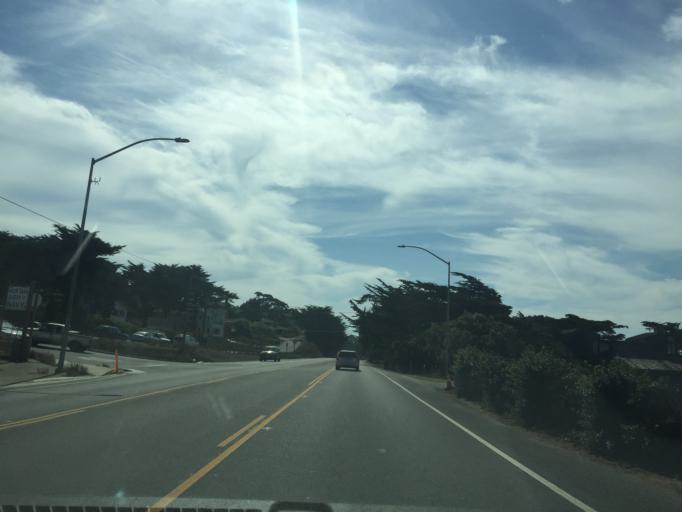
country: US
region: California
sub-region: San Mateo County
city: Montara
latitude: 37.5414
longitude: -122.5164
